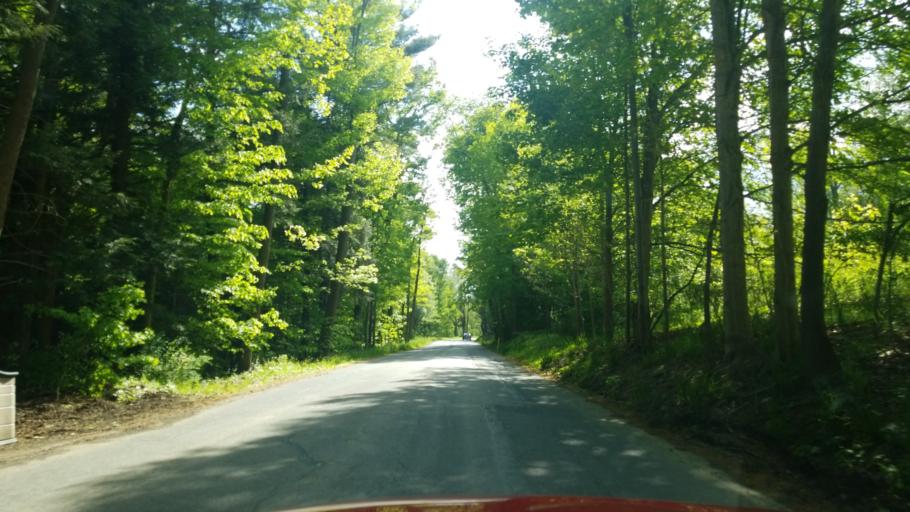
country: US
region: Pennsylvania
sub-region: Clearfield County
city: Hyde
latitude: 40.9775
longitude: -78.4741
